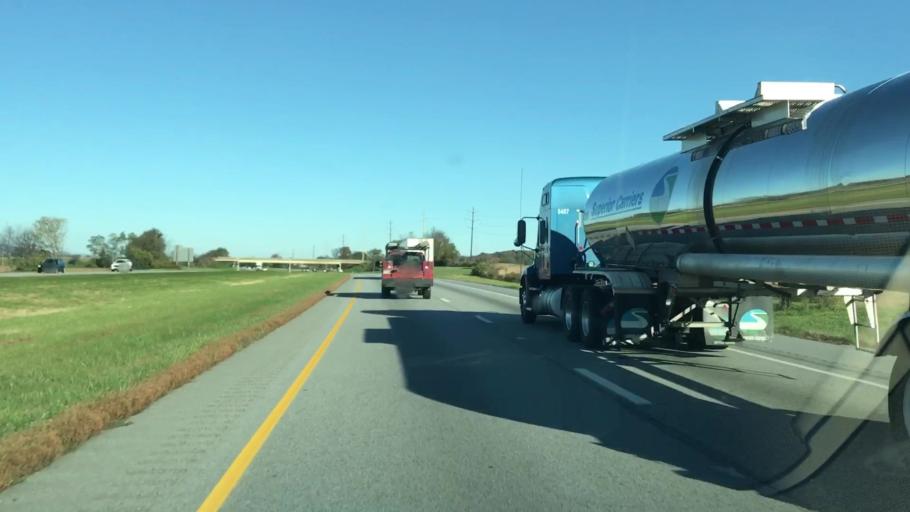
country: US
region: Pennsylvania
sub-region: Cumberland County
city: Schlusser
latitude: 40.2433
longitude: -77.0934
